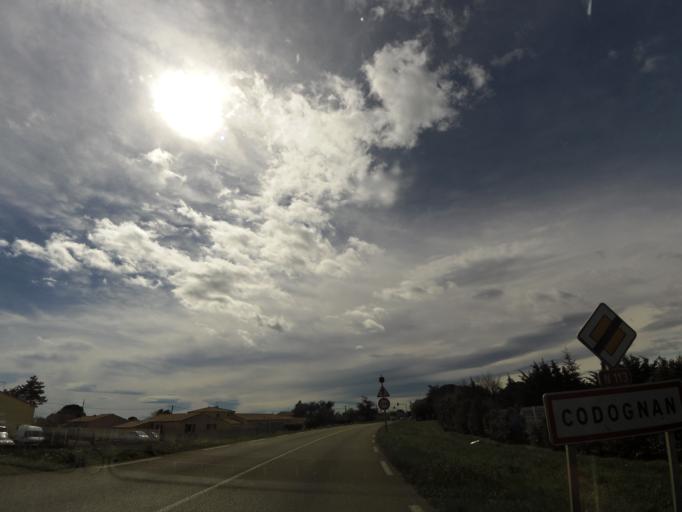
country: FR
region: Languedoc-Roussillon
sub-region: Departement du Gard
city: Codognan
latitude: 43.7294
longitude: 4.2258
